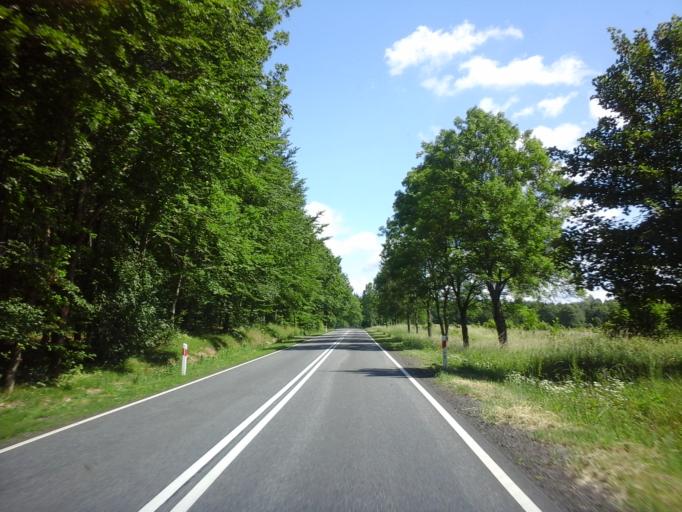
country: PL
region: West Pomeranian Voivodeship
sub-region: Powiat stargardzki
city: Insko
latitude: 53.4783
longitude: 15.5804
